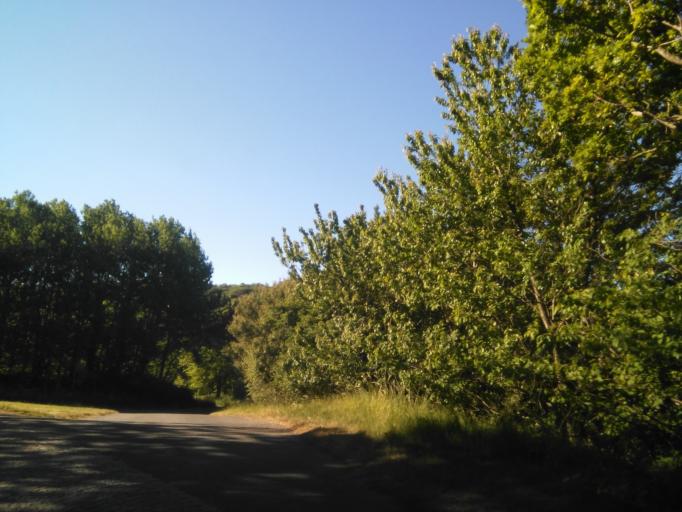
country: DK
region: Capital Region
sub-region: Bornholm Kommune
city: Ronne
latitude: 55.2793
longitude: 14.7598
